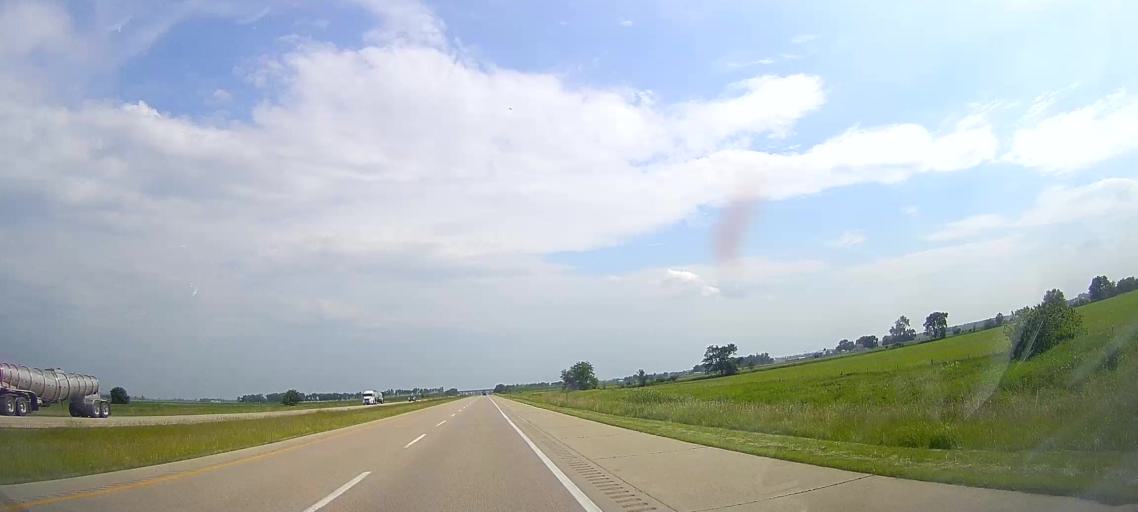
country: US
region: Iowa
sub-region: Monona County
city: Onawa
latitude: 41.8963
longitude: -96.1044
